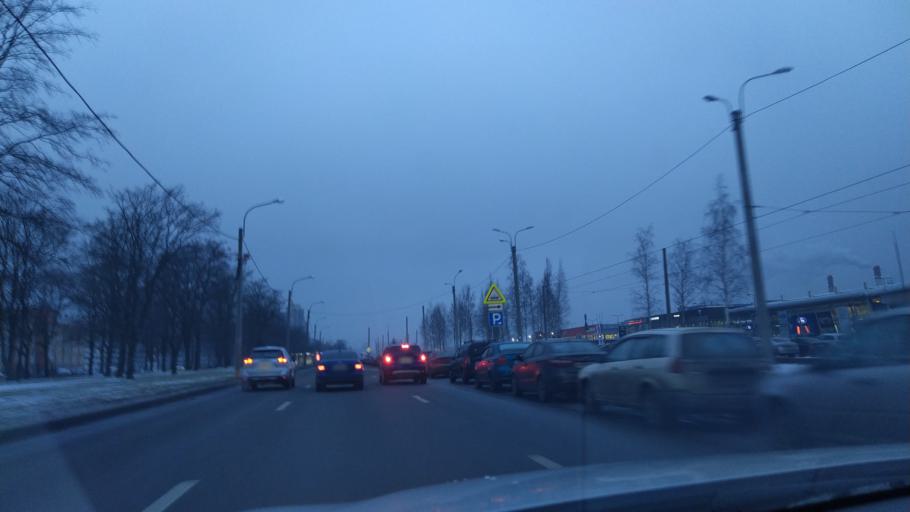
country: RU
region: St.-Petersburg
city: Grazhdanka
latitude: 60.0231
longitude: 30.4323
